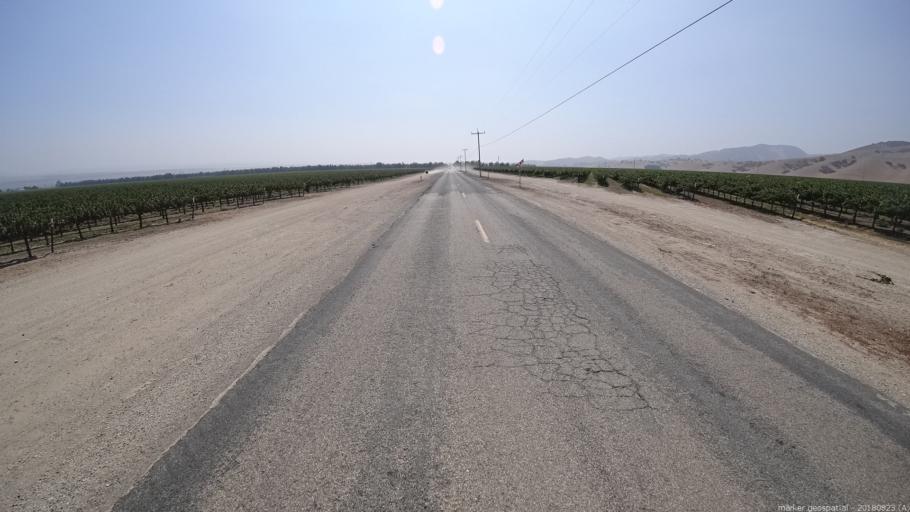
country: US
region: California
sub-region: Monterey County
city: Greenfield
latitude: 36.2537
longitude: -121.2002
